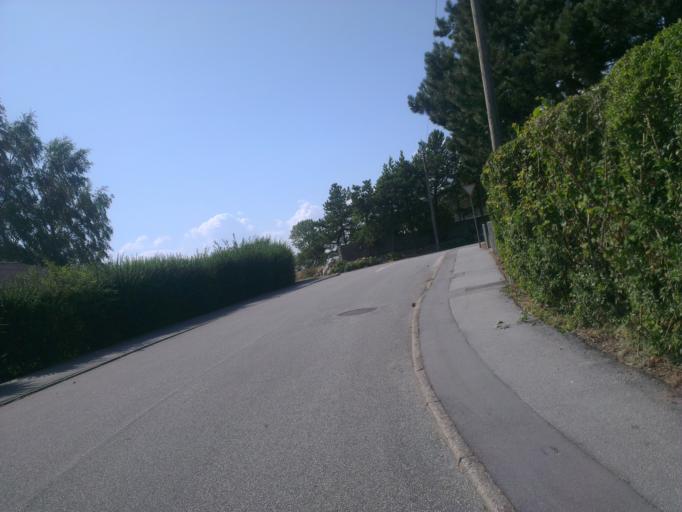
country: DK
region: Capital Region
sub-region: Frederikssund Kommune
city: Skibby
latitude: 55.7746
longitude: 12.0223
